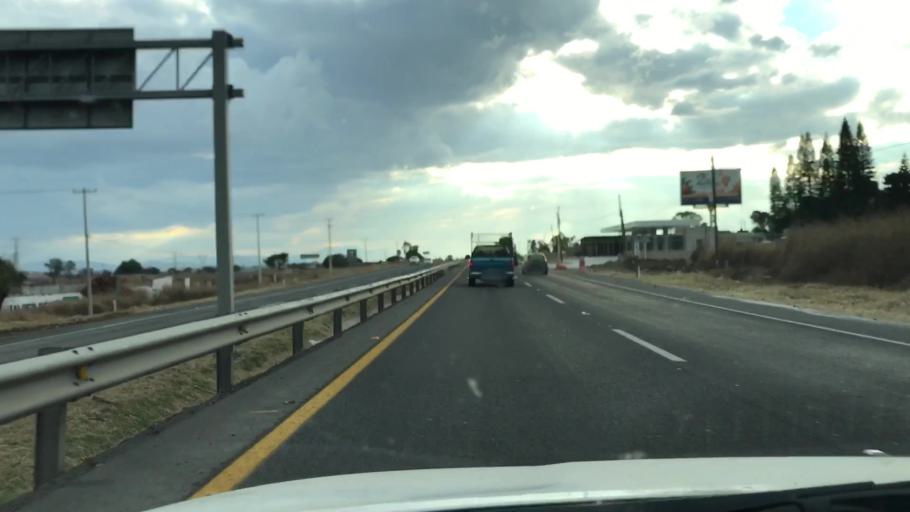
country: MX
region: Guanajuato
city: Penjamo
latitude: 20.4130
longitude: -101.7329
